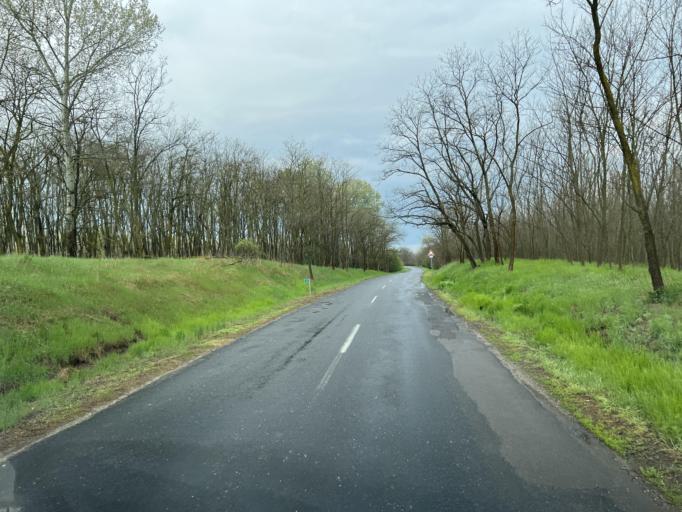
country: HU
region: Pest
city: Ujhartyan
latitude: 47.2276
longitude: 19.4234
